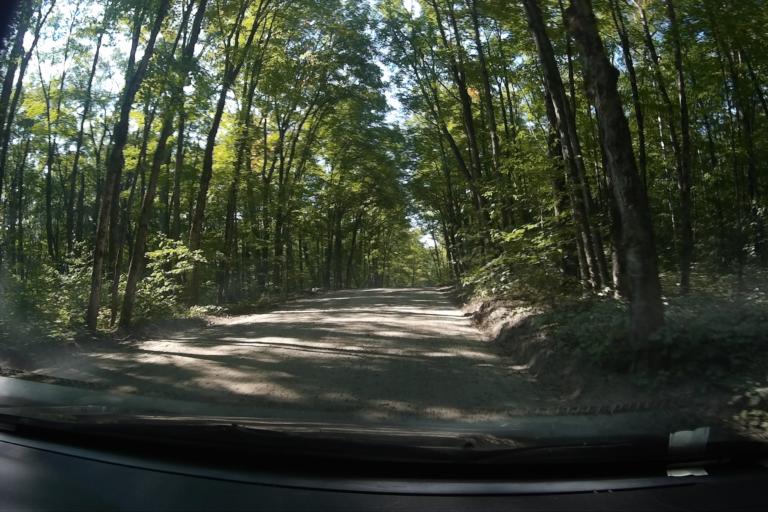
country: CA
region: Ontario
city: Huntsville
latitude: 45.5578
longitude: -78.6953
